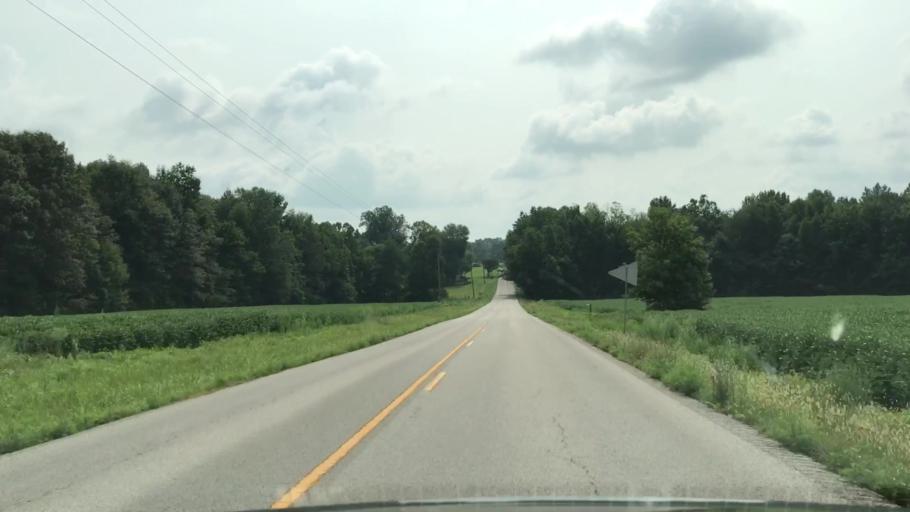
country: US
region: Kentucky
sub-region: Edmonson County
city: Brownsville
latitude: 37.1430
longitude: -86.1887
